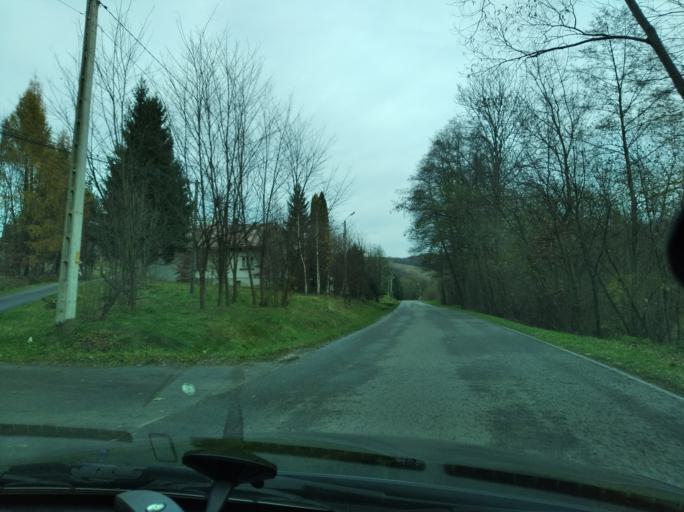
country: PL
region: Subcarpathian Voivodeship
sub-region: Powiat ropczycko-sedziszowski
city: Iwierzyce
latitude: 49.9466
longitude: 21.7398
